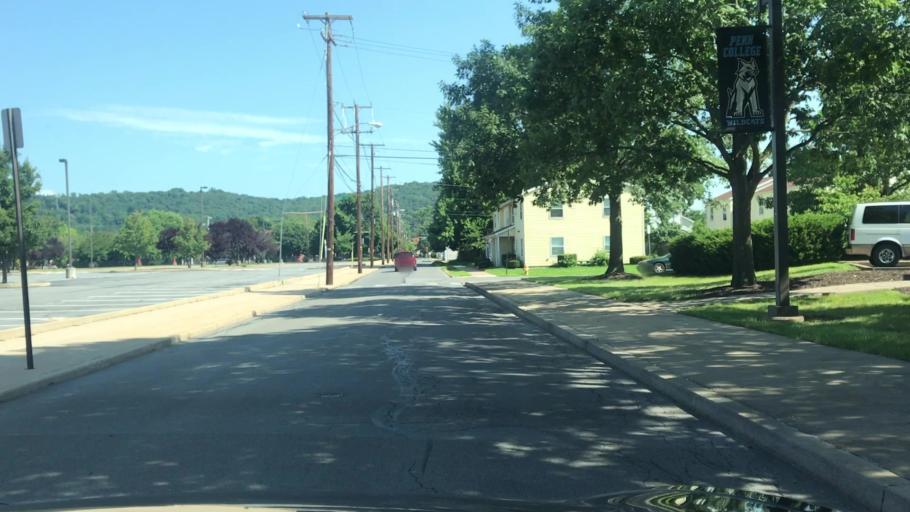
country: US
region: Pennsylvania
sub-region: Lycoming County
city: Duboistown
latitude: 41.2353
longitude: -77.0228
